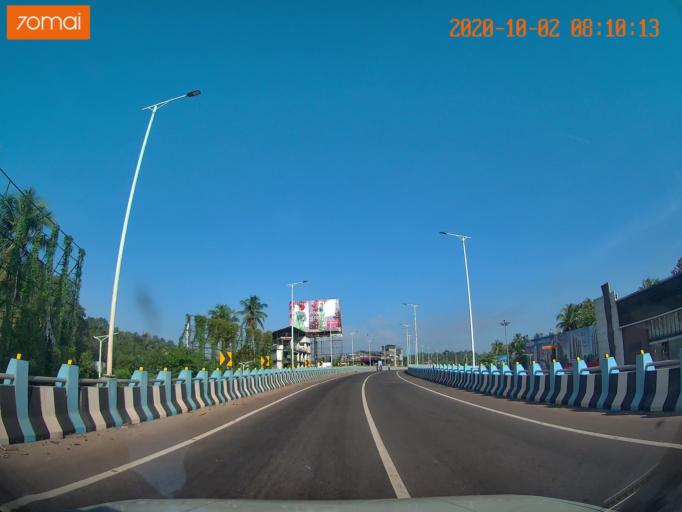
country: IN
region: Kerala
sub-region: Kozhikode
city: Kozhikode
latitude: 11.2640
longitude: 75.8125
